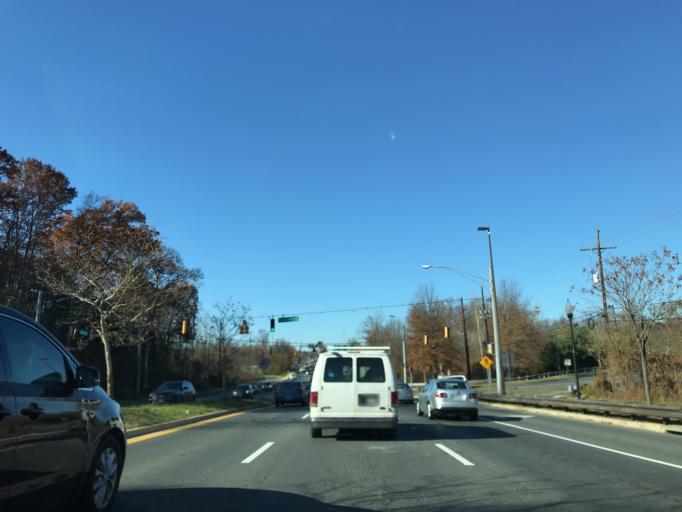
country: US
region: Maryland
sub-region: Montgomery County
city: Rockville
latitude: 39.0555
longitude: -77.1485
